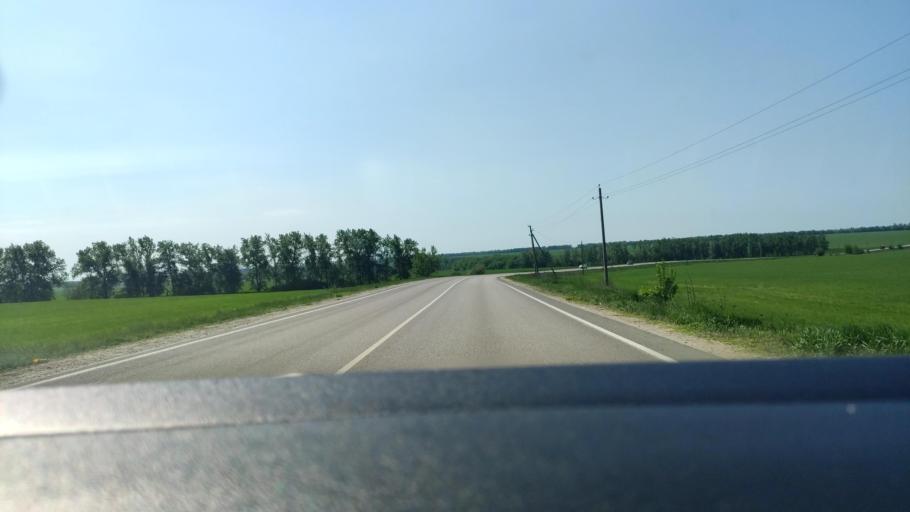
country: RU
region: Voronezj
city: Novaya Usman'
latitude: 51.5582
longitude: 39.3761
